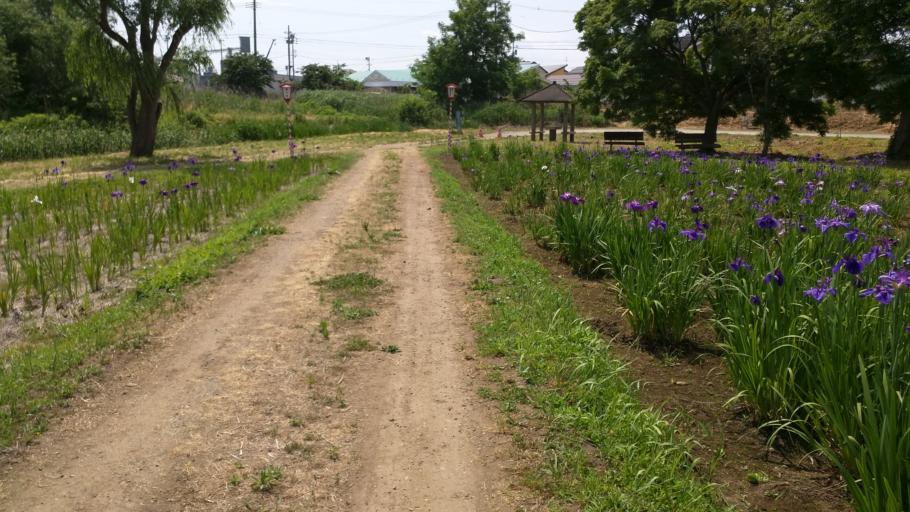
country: JP
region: Fukushima
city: Kitakata
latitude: 37.5966
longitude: 139.8821
